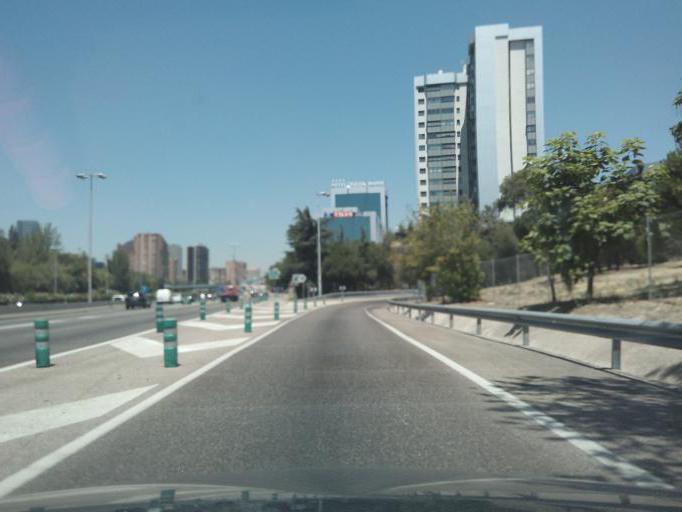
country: ES
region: Madrid
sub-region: Provincia de Madrid
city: Chamartin
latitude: 40.4671
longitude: -3.6682
